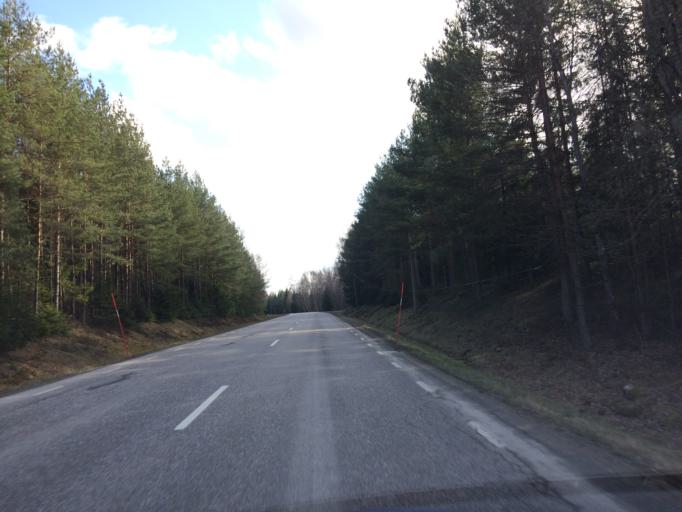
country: SE
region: Kronoberg
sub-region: Almhults Kommun
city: AElmhult
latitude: 56.5913
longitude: 14.0979
